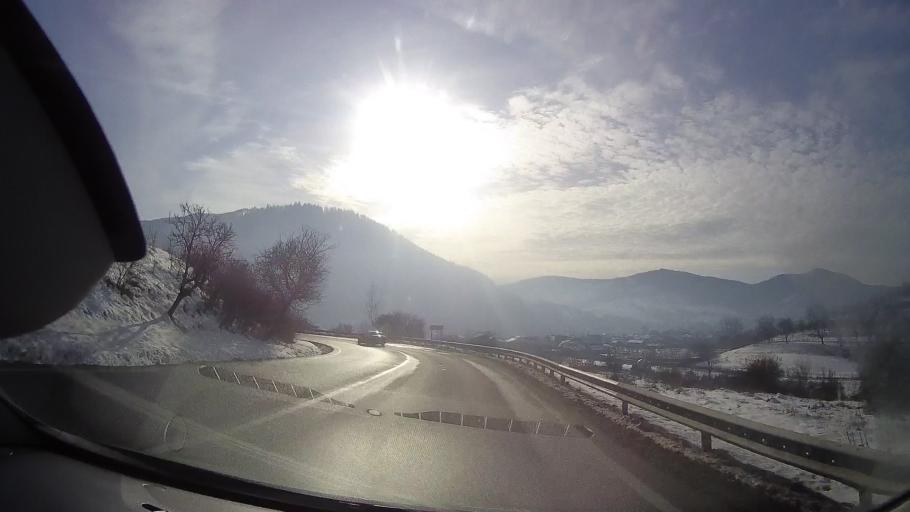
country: RO
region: Neamt
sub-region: Comuna Garcina
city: Garcina
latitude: 46.9784
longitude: 26.3577
